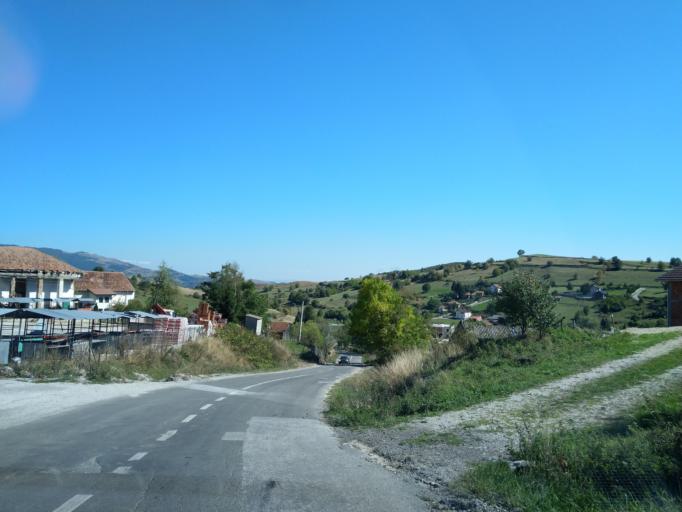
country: RS
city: Sokolovica
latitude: 43.2496
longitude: 20.2283
